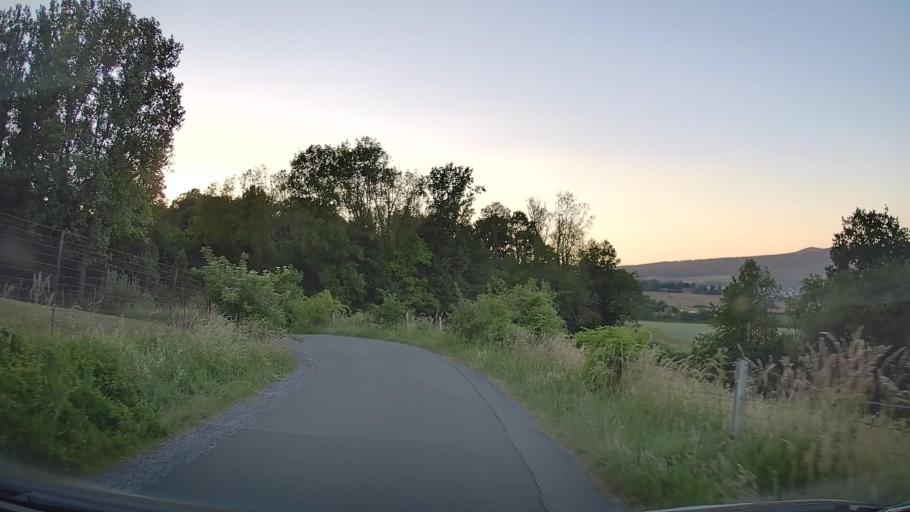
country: DE
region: North Rhine-Westphalia
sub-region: Regierungsbezirk Detmold
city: Lugde
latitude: 51.9646
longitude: 9.2254
